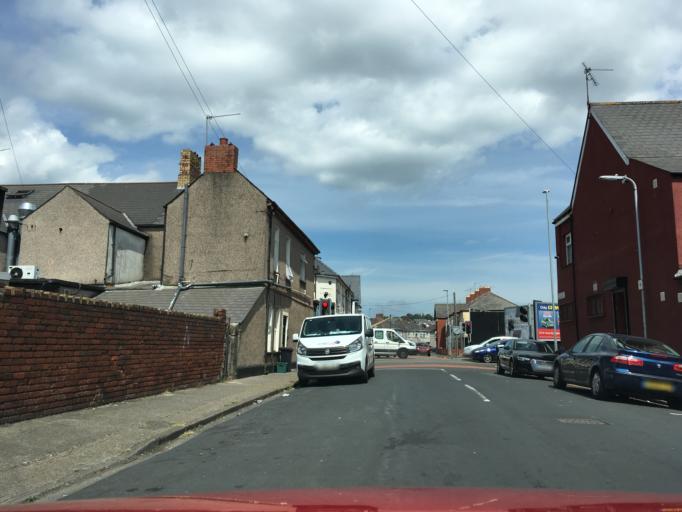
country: GB
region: Wales
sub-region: Newport
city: Newport
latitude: 51.5818
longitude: -2.9738
